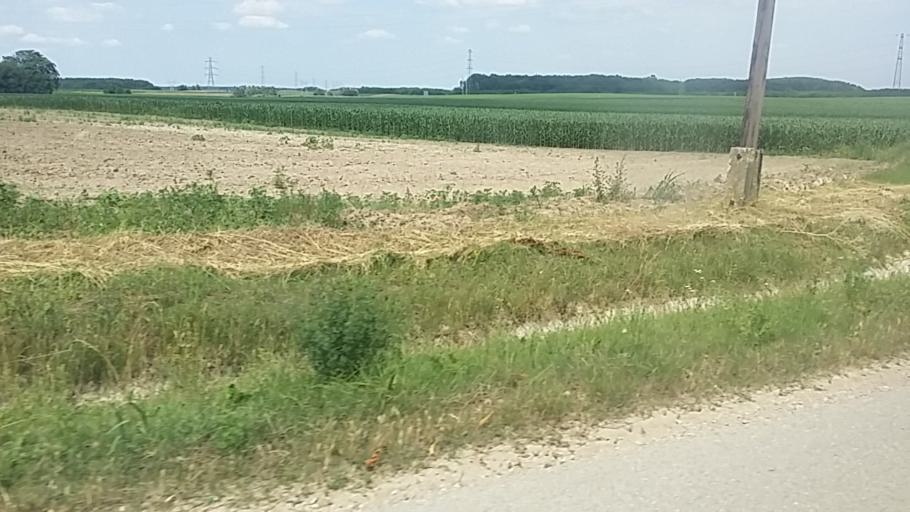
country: HU
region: Tolna
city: Szedres
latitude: 46.4750
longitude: 18.6948
